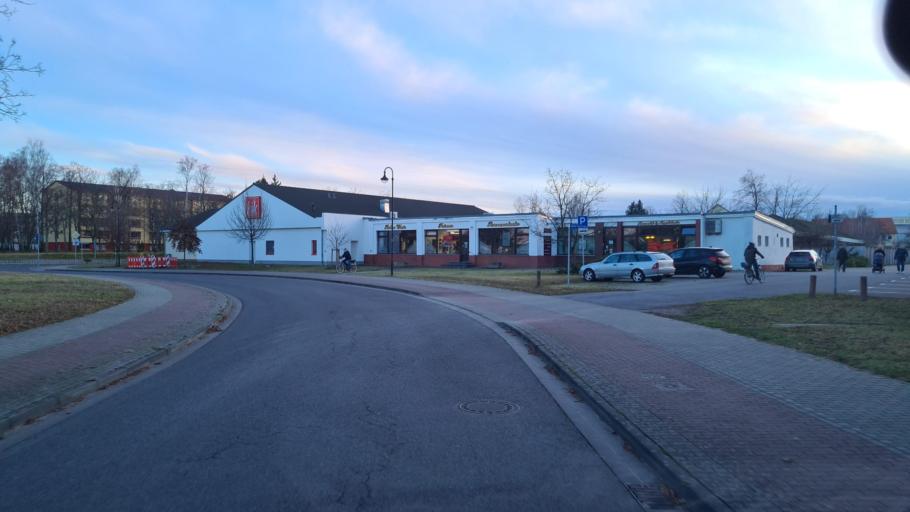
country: DE
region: Brandenburg
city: Vetschau
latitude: 51.7846
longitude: 14.0868
